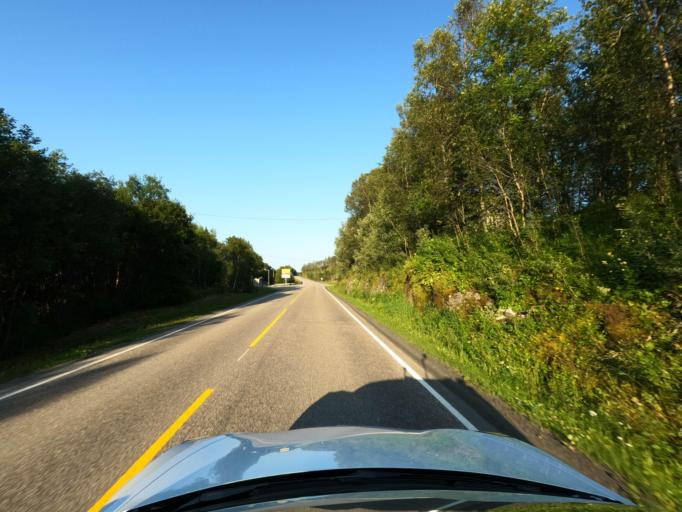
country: NO
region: Troms
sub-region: Skanland
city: Evenskjer
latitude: 68.4926
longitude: 16.7286
